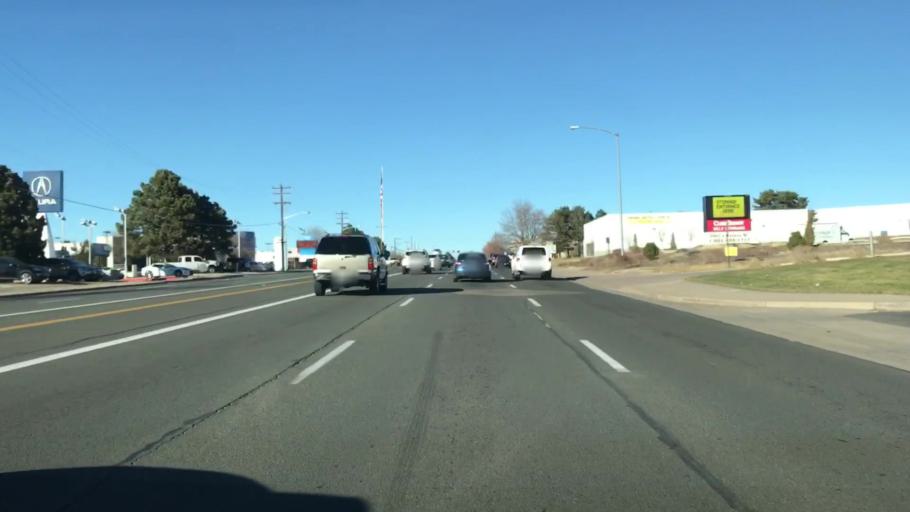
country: US
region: Colorado
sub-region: Adams County
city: Aurora
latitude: 39.6638
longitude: -104.8662
